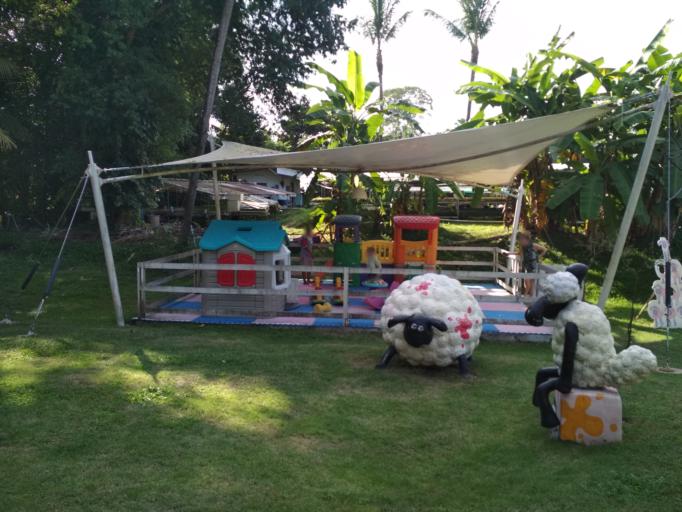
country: TH
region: Surat Thani
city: Ko Samui
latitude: 9.5619
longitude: 99.9968
